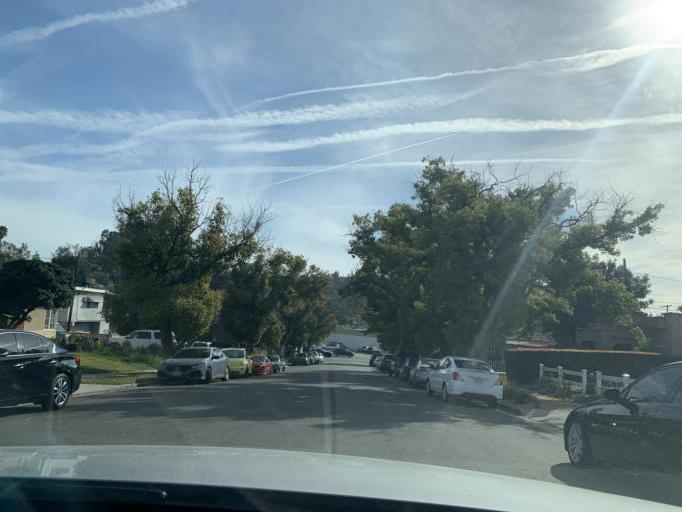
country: US
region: California
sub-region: Los Angeles County
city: Glendale
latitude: 34.1427
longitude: -118.2215
